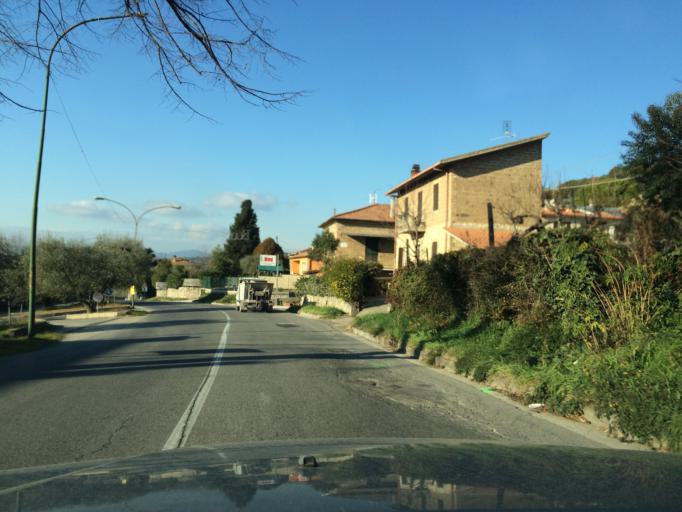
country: IT
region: Umbria
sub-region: Provincia di Terni
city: Fornole
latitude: 42.5430
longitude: 12.4548
